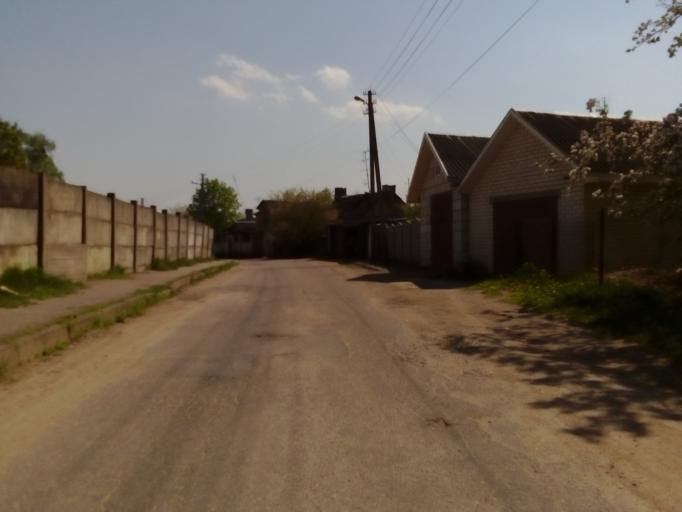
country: BY
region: Grodnenskaya
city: Hrodna
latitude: 53.6663
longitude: 23.8488
